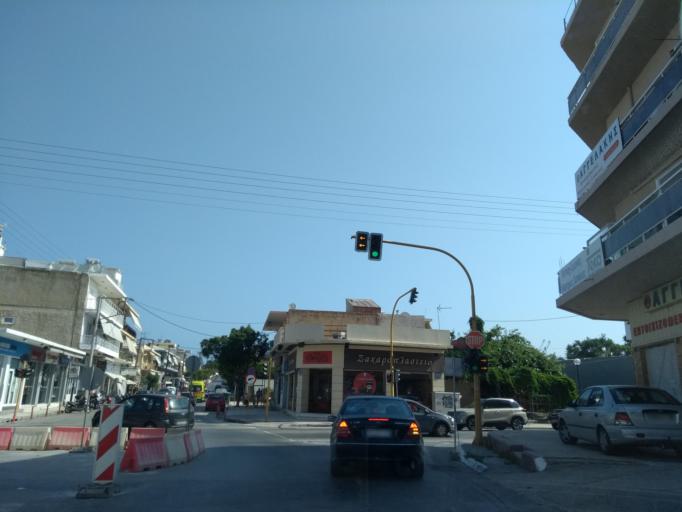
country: GR
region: Crete
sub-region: Nomos Chanias
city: Chania
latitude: 35.5039
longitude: 24.0198
